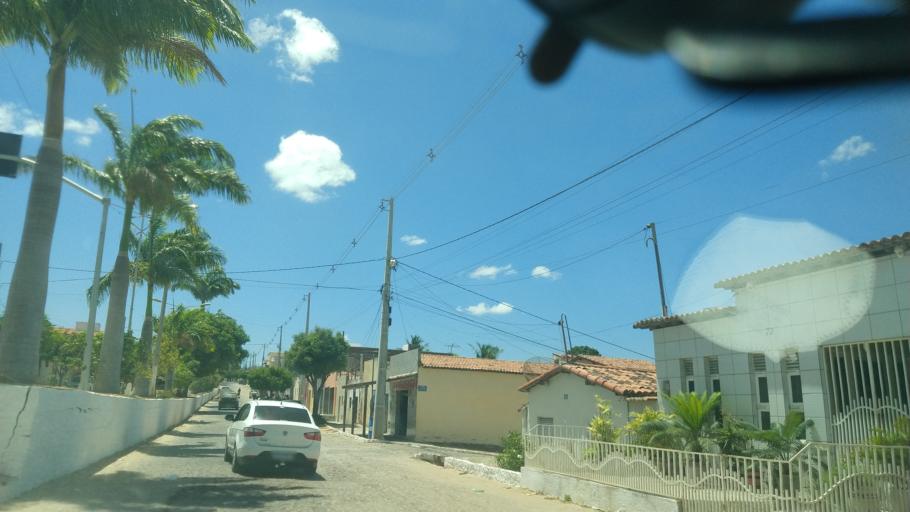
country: BR
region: Rio Grande do Norte
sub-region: Cerro Cora
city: Cerro Cora
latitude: -6.0478
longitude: -36.3500
